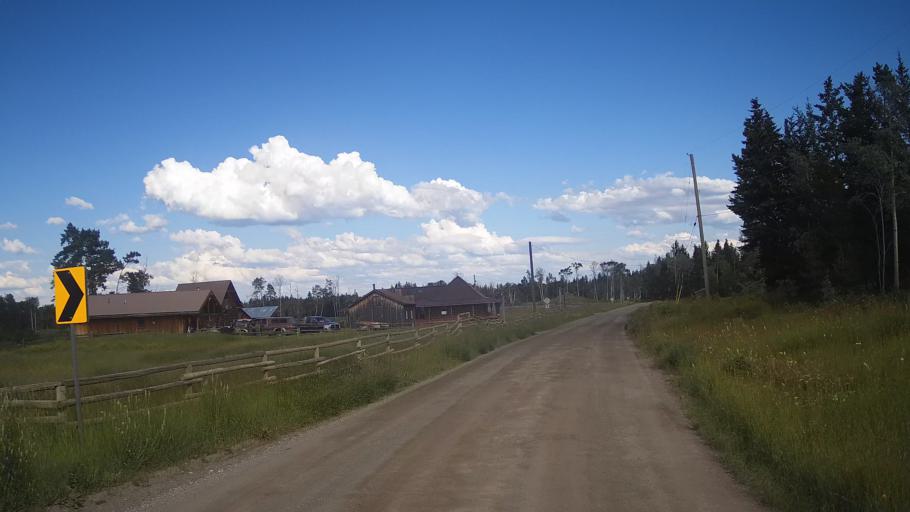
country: CA
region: British Columbia
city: Cache Creek
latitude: 51.1815
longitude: -121.5821
